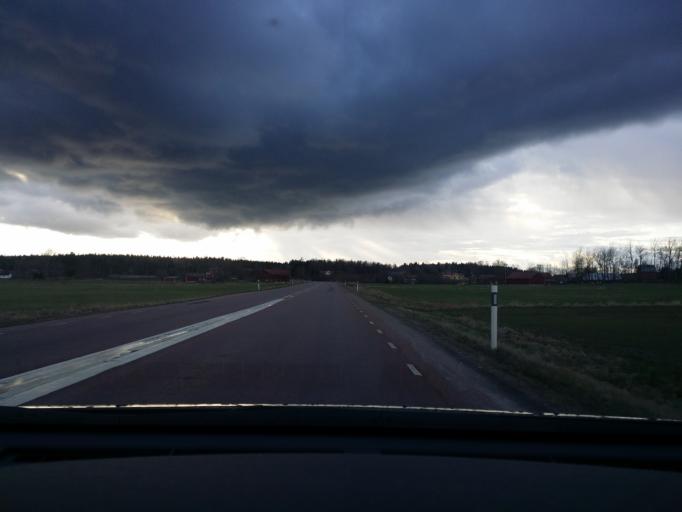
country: SE
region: Soedermanland
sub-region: Eskilstuna Kommun
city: Arla
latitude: 59.3890
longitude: 16.6438
